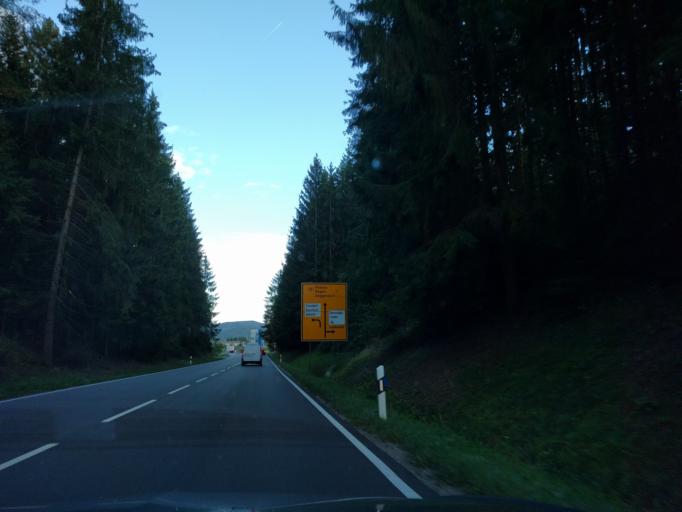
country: DE
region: Bavaria
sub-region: Lower Bavaria
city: Patersdorf
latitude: 49.0298
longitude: 12.9655
